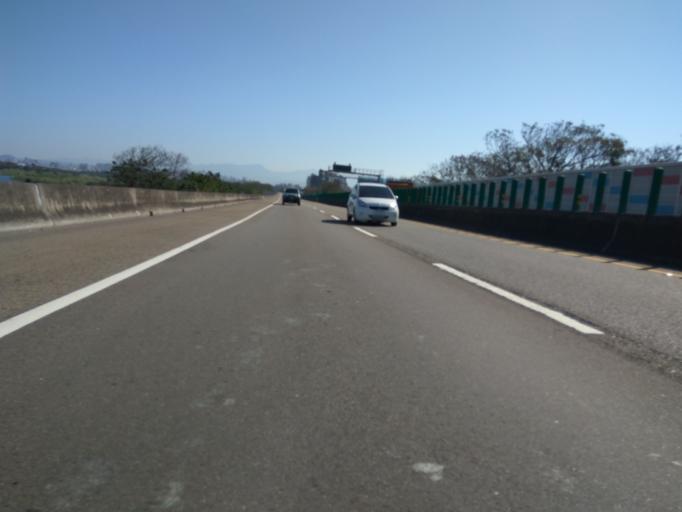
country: TW
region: Taiwan
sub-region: Hsinchu
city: Hsinchu
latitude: 24.8300
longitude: 120.9595
